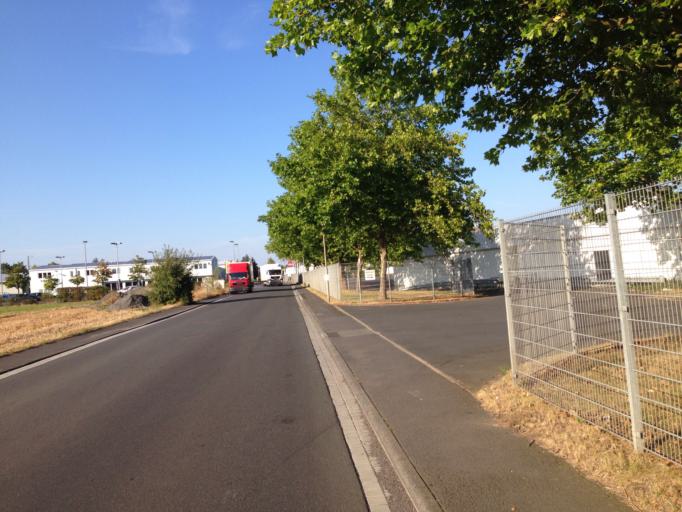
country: DE
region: Hesse
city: Lollar
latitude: 50.6391
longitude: 8.6984
